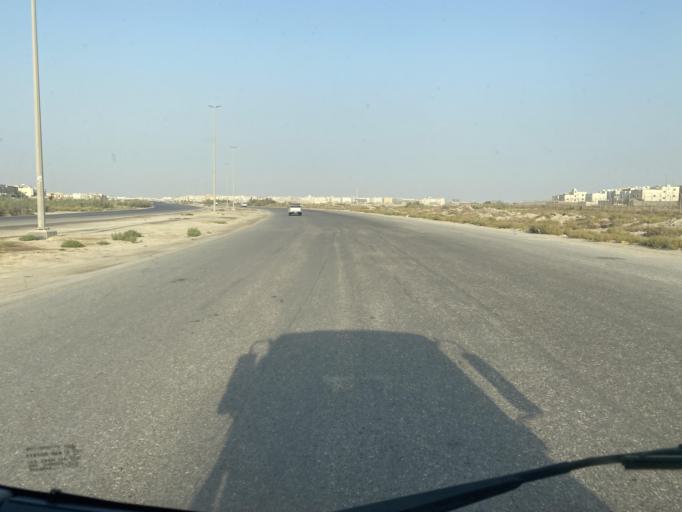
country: SA
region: Eastern Province
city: Sayhat
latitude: 26.4014
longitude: 49.9887
